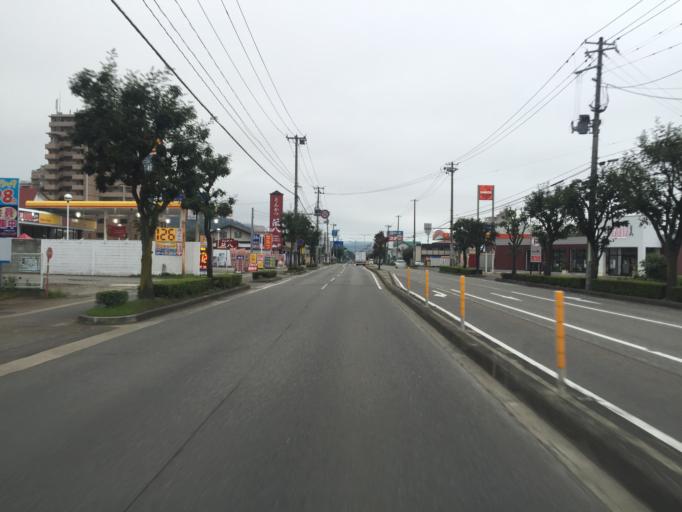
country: JP
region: Fukushima
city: Kitakata
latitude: 37.4961
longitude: 139.9427
